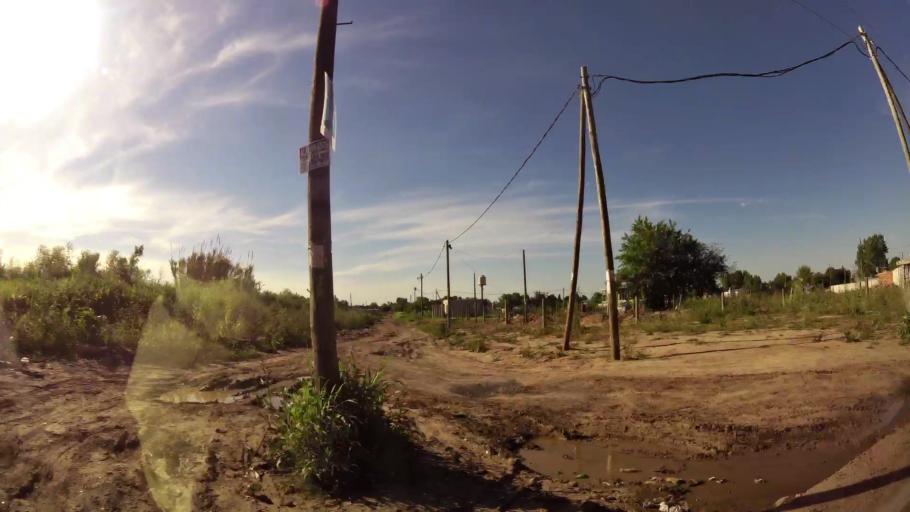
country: AR
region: Buenos Aires
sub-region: Partido de Almirante Brown
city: Adrogue
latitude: -34.8277
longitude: -58.3544
